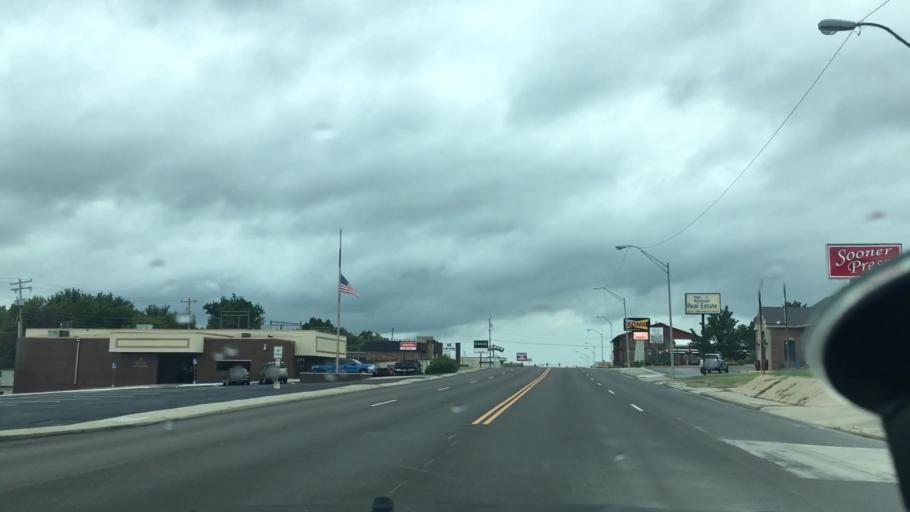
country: US
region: Oklahoma
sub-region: Seminole County
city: Seminole
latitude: 35.2301
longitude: -96.6711
